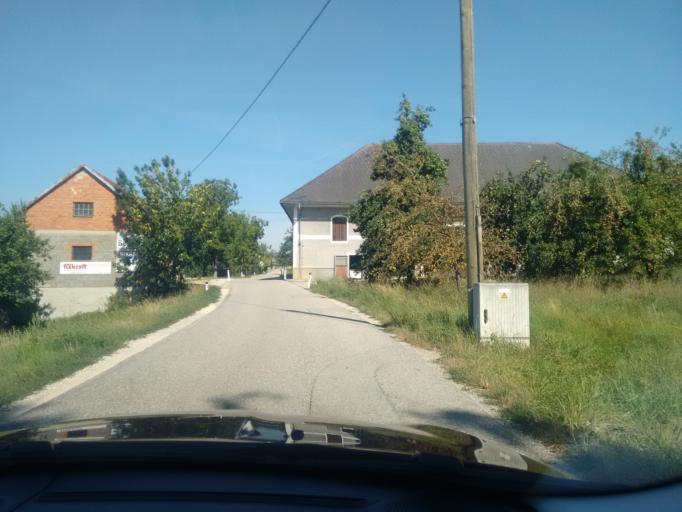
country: AT
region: Upper Austria
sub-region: Wels-Land
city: Steinhaus
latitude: 48.1112
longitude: 14.0238
